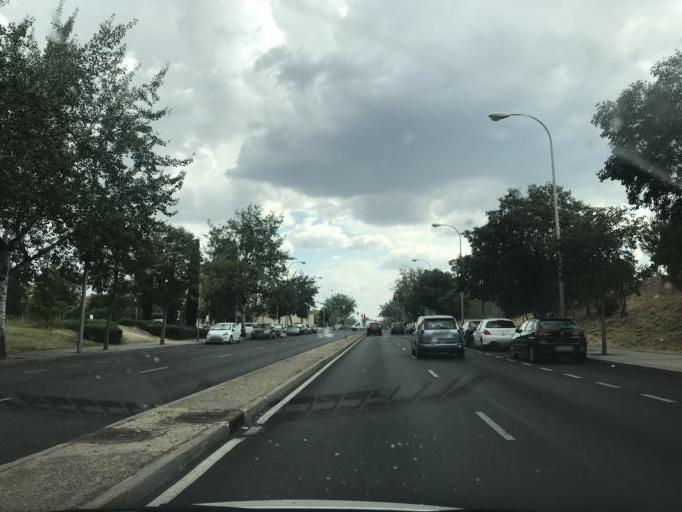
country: ES
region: Madrid
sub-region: Provincia de Madrid
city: Hortaleza
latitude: 40.4802
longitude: -3.6511
